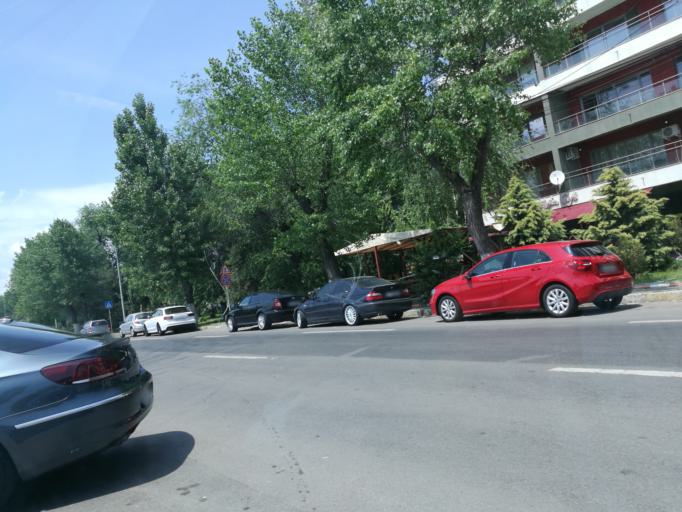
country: RO
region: Constanta
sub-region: Municipiul Constanta
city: Palazu Mare
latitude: 44.2184
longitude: 28.6343
